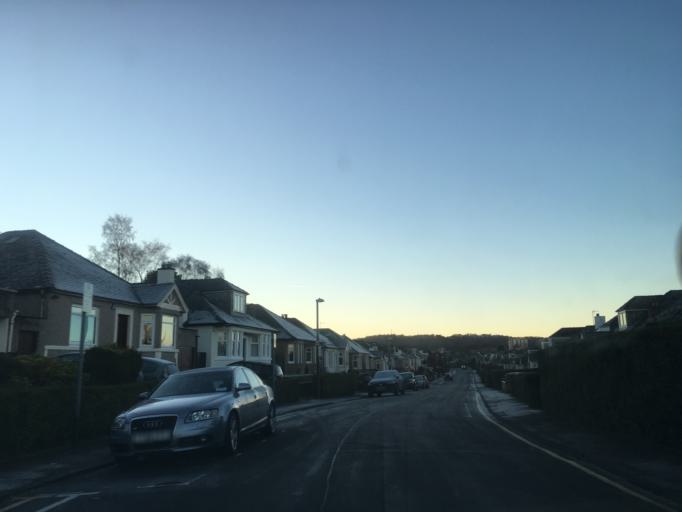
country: GB
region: Scotland
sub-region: Edinburgh
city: Edinburgh
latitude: 55.9539
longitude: -3.2306
